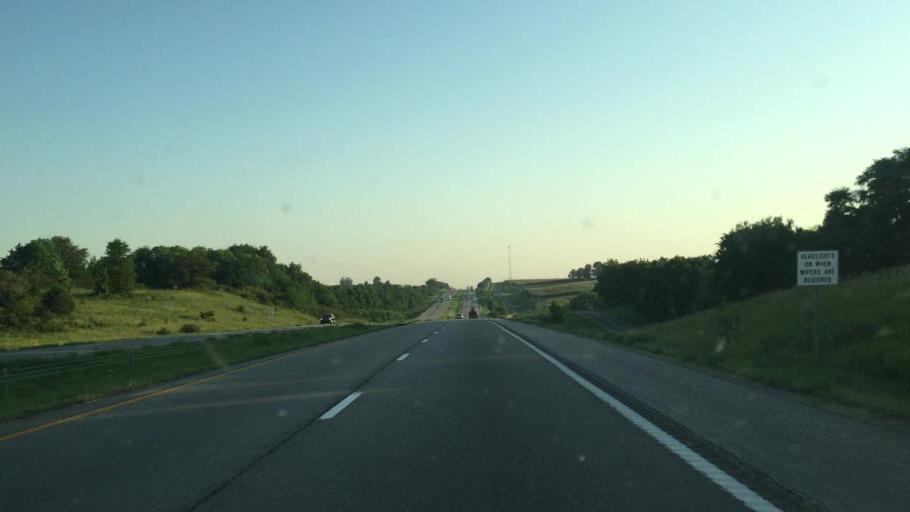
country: US
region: Missouri
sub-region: Platte County
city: Platte City
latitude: 39.5361
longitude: -94.7873
